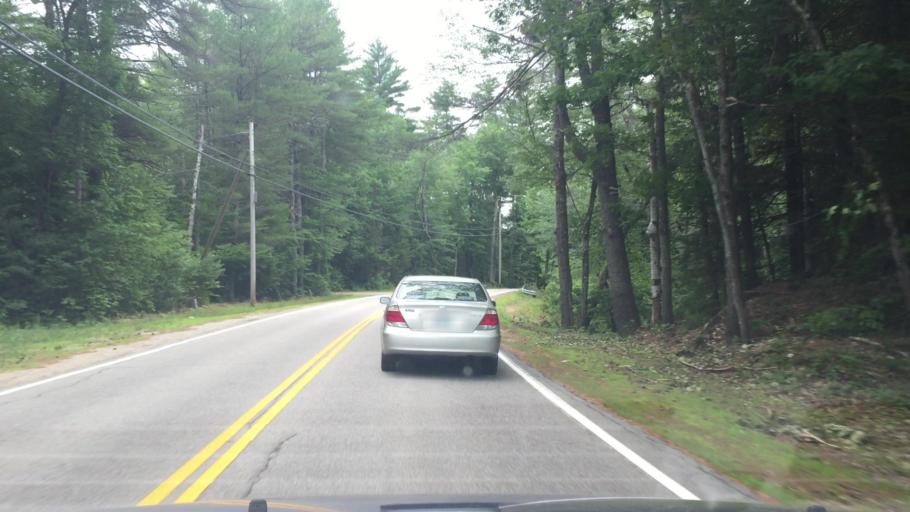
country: US
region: New Hampshire
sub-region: Carroll County
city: Madison
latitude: 43.9172
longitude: -71.0734
